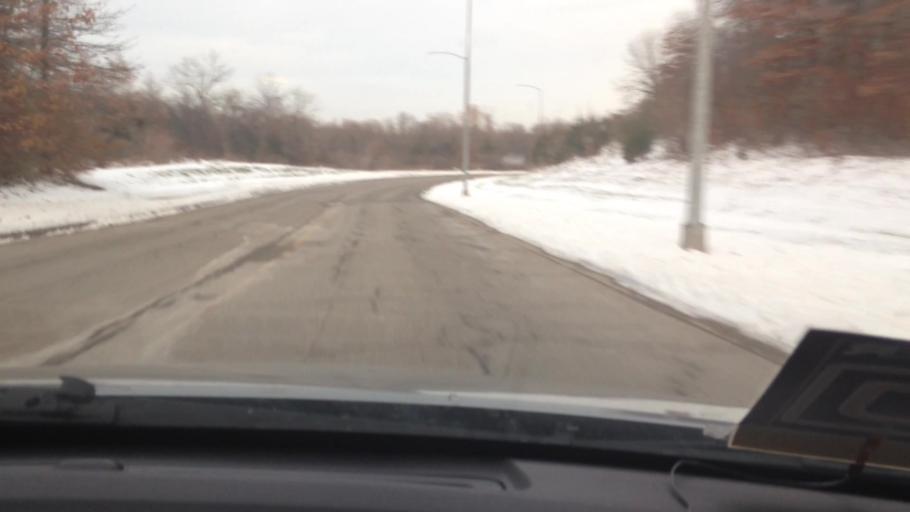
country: US
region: Kansas
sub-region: Leavenworth County
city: Lansing
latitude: 39.2457
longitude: -94.9149
